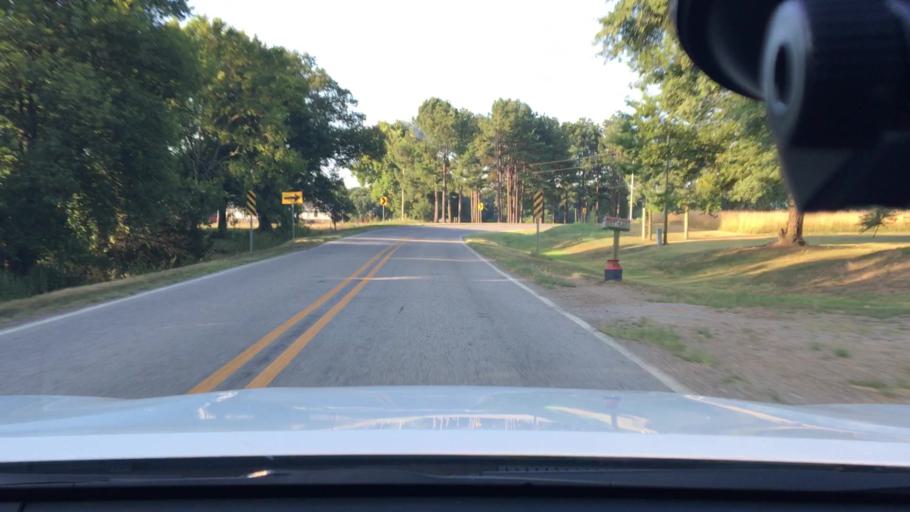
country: US
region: Arkansas
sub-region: Johnson County
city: Coal Hill
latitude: 35.3420
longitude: -93.5963
